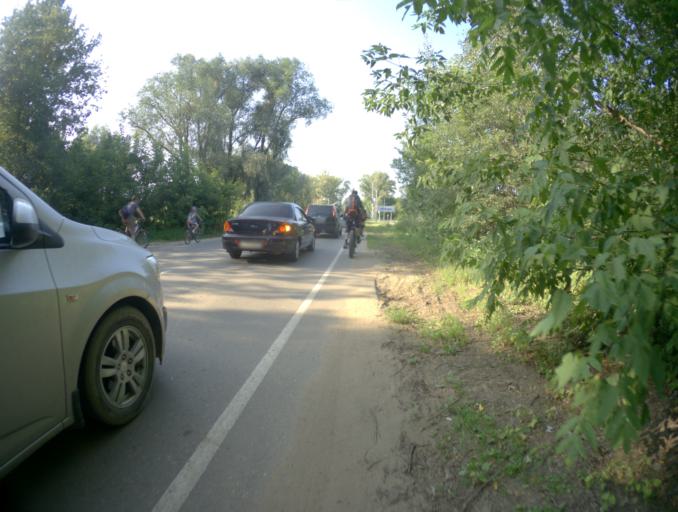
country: RU
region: Nizjnij Novgorod
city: Bor
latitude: 56.3548
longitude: 44.0516
